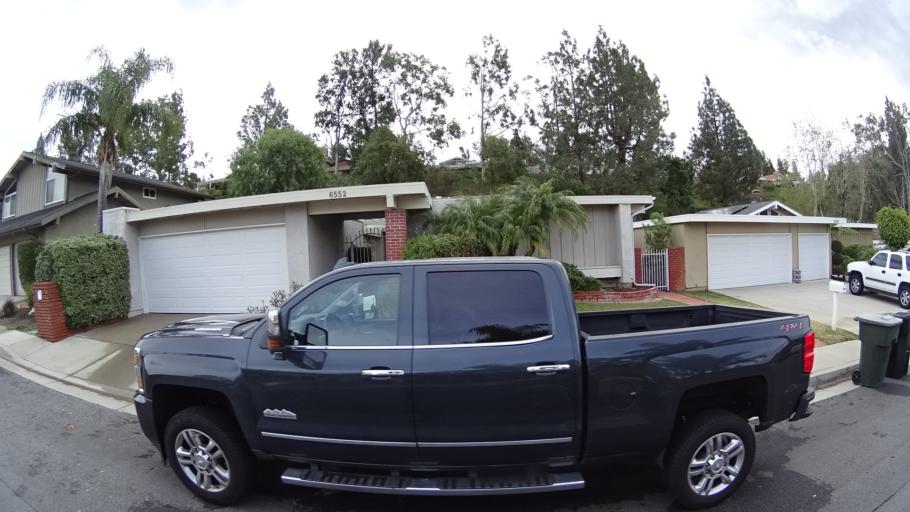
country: US
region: California
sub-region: Orange County
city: Villa Park
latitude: 33.8491
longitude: -117.7654
